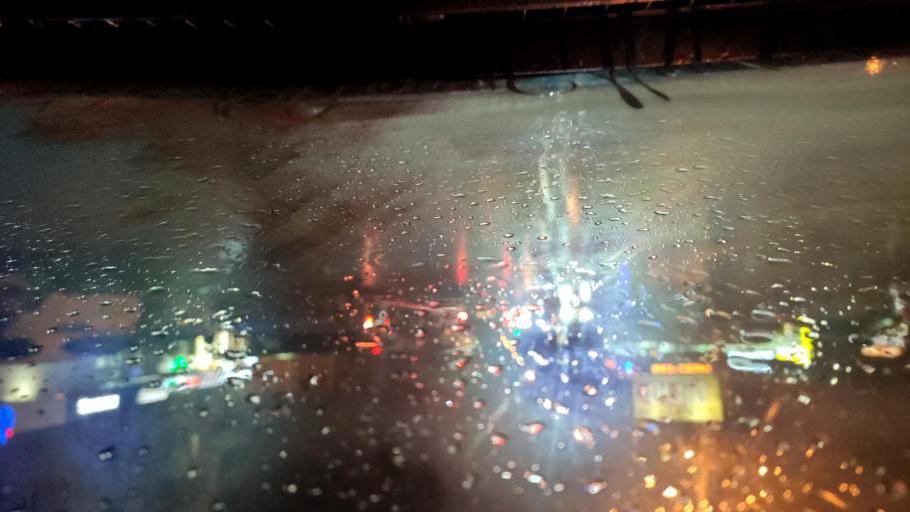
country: RU
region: Voronezj
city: Voronezh
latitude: 51.6742
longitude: 39.1559
